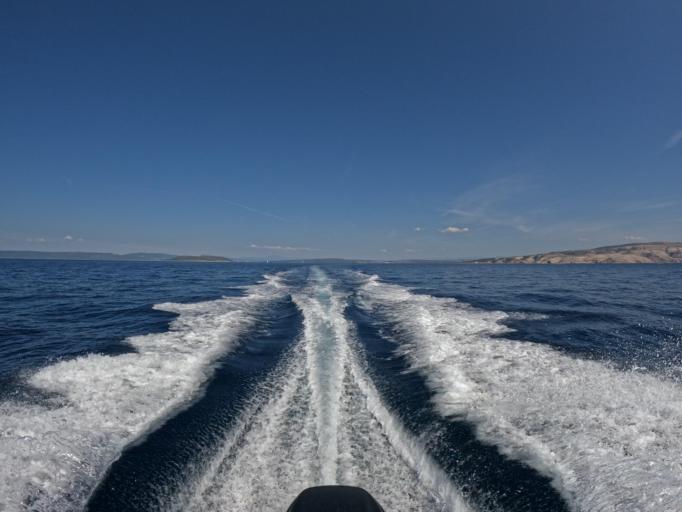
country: HR
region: Primorsko-Goranska
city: Punat
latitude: 44.9192
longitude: 14.6229
